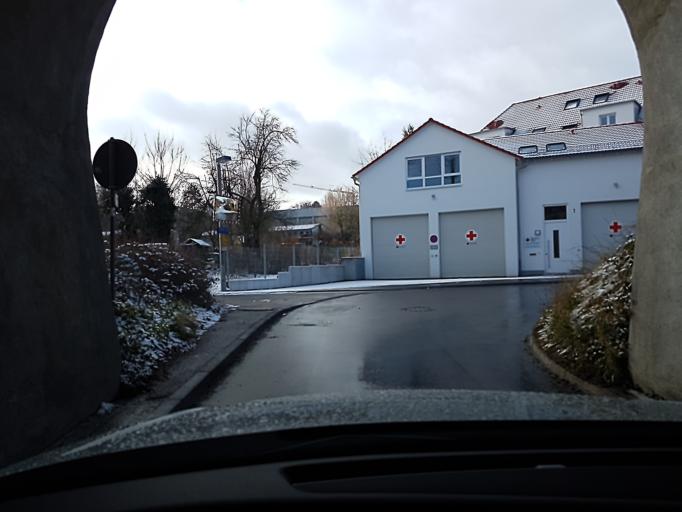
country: DE
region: Baden-Wuerttemberg
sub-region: Regierungsbezirk Stuttgart
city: Weinsberg
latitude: 49.1500
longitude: 9.2806
